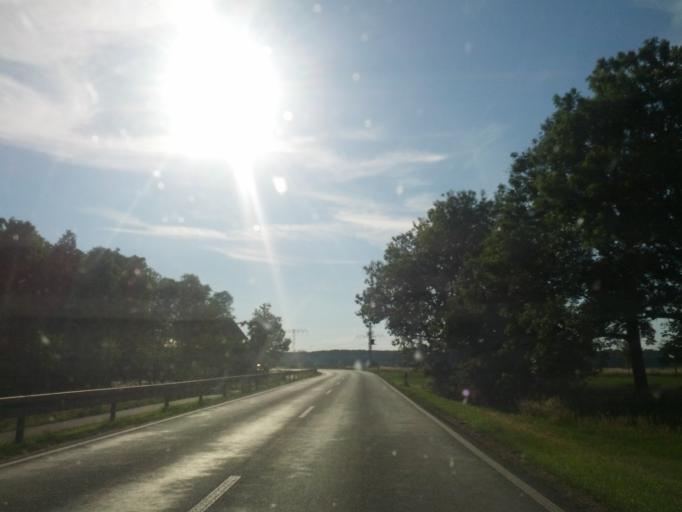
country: DE
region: Thuringia
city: Schwabhausen
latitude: 50.8904
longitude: 10.7598
